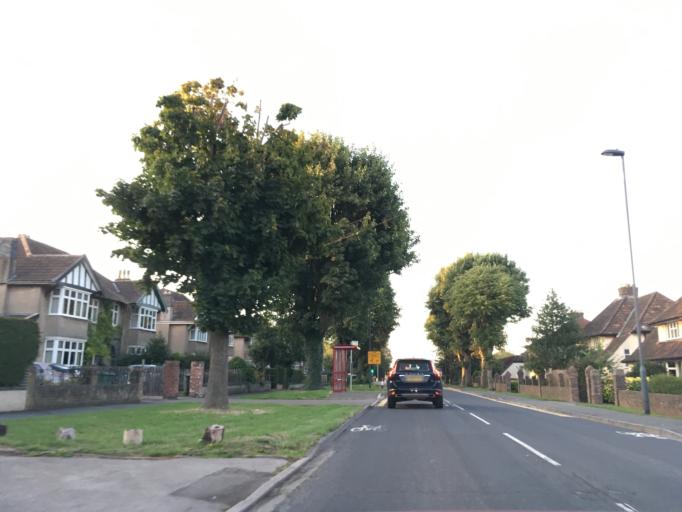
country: GB
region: England
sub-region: South Gloucestershire
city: Mangotsfield
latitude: 51.4915
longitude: -2.5103
